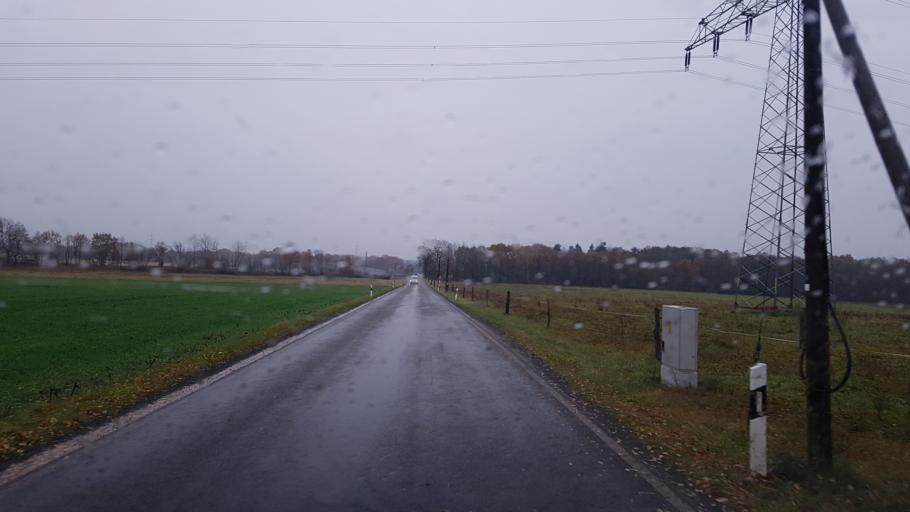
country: DE
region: Brandenburg
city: Altdobern
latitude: 51.6621
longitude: 14.0009
